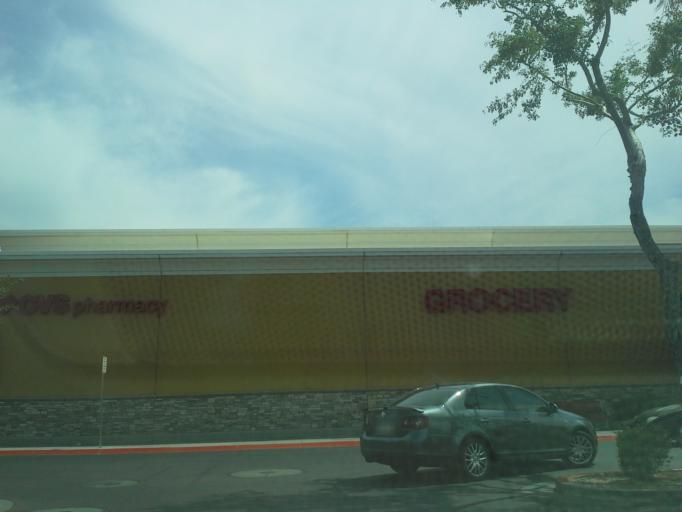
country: US
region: Arizona
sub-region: Maricopa County
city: Glendale
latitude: 33.6388
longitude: -112.0685
